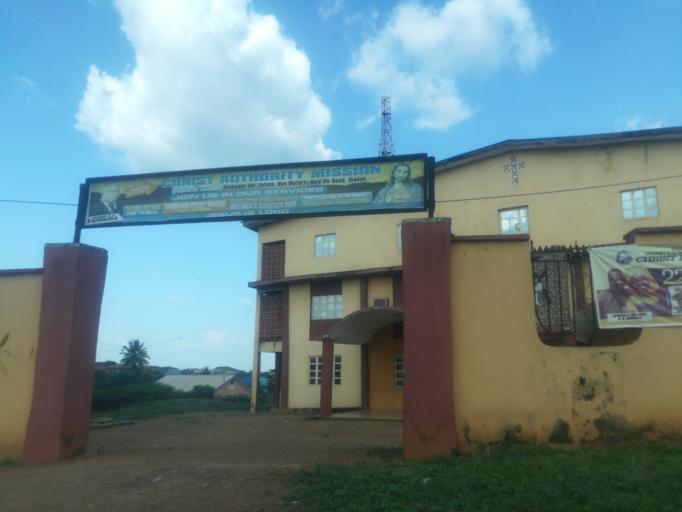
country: NG
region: Oyo
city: Ibadan
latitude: 7.4023
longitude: 3.9618
